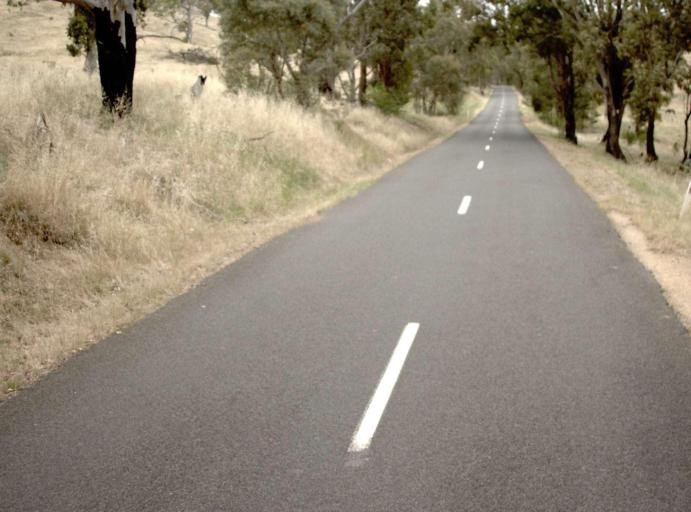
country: AU
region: Victoria
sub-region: Wellington
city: Heyfield
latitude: -37.6772
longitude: 146.6552
